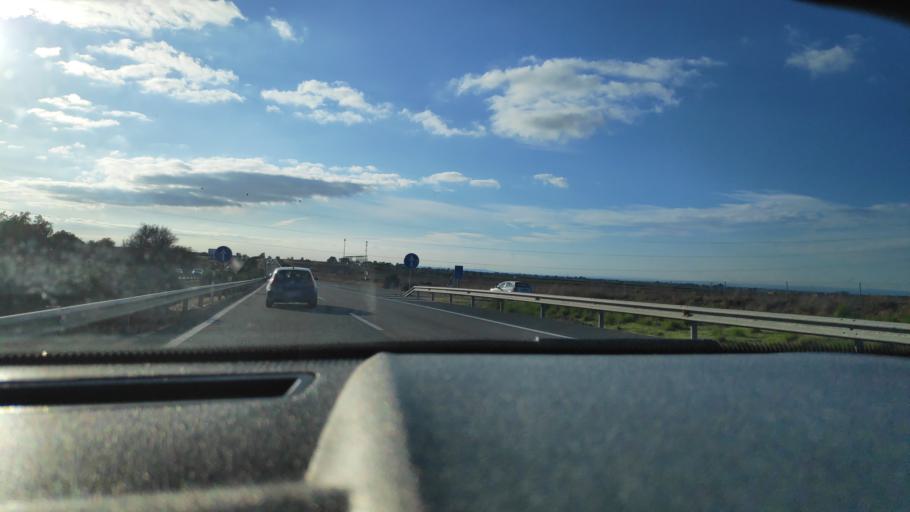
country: ES
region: Andalusia
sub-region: Provincia de Sevilla
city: Carmona
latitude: 37.4683
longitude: -5.7151
